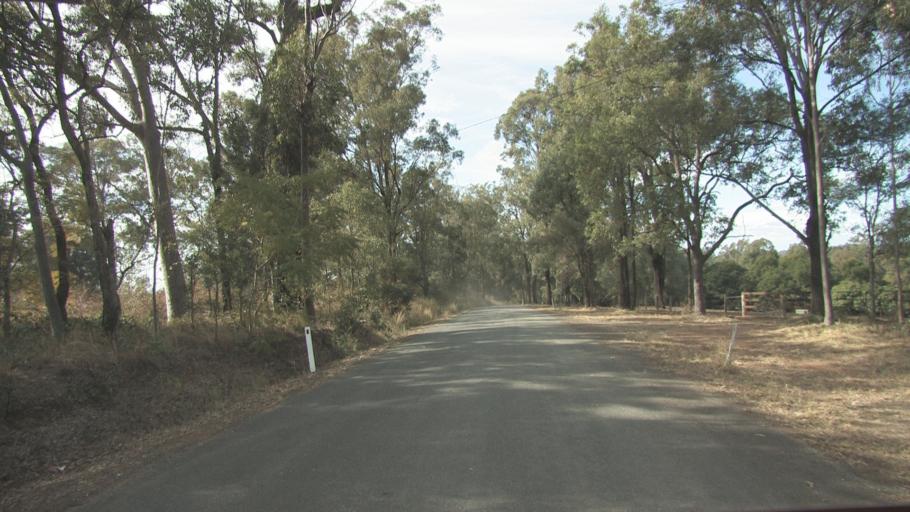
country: AU
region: Queensland
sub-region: Logan
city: Cedar Vale
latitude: -27.8967
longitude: 152.9886
